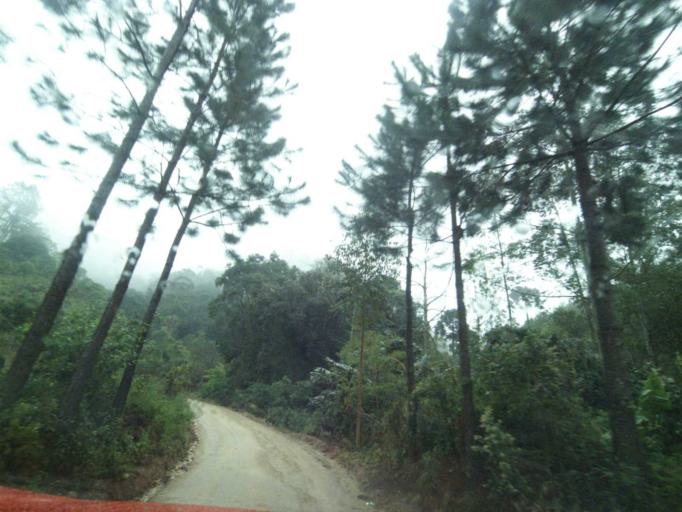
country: BR
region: Santa Catarina
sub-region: Anitapolis
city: Anitapolis
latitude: -27.8954
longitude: -49.1932
